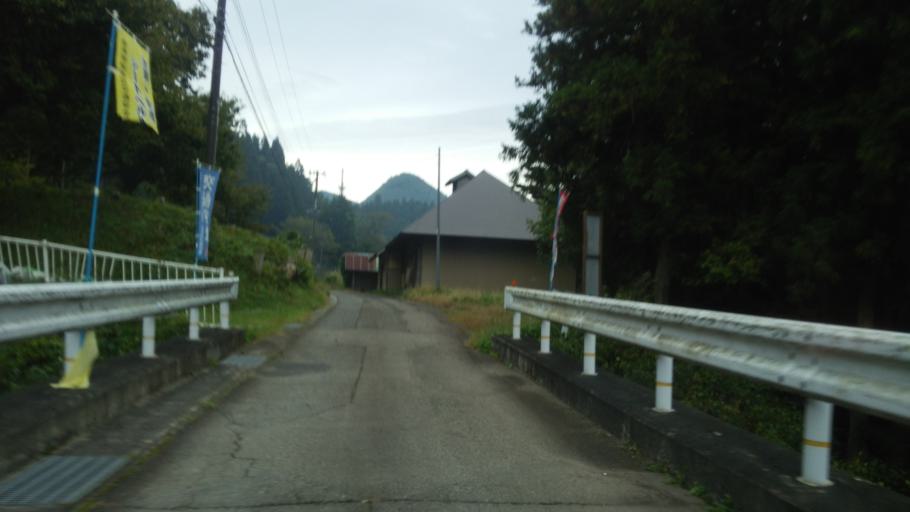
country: JP
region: Fukushima
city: Inawashiro
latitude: 37.3717
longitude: 139.9661
